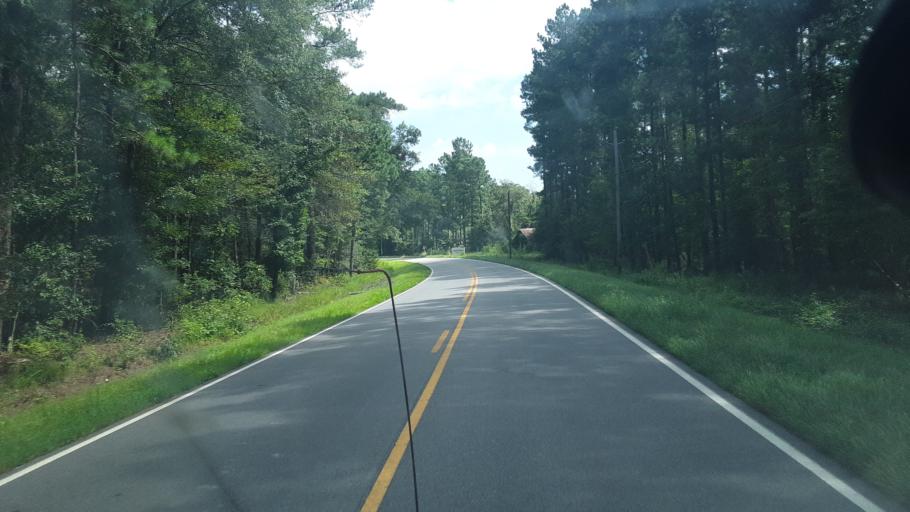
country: US
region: South Carolina
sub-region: Bamberg County
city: Bamberg
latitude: 33.0859
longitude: -81.0154
